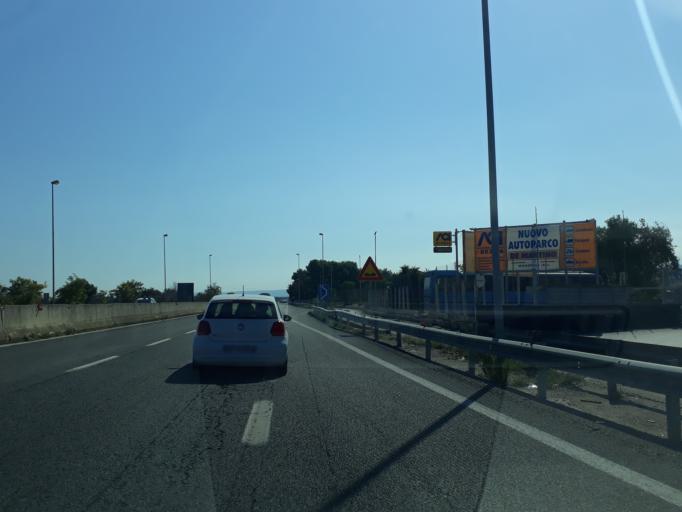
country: IT
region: Apulia
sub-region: Provincia di Bari
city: Monopoli
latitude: 40.9177
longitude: 17.3186
